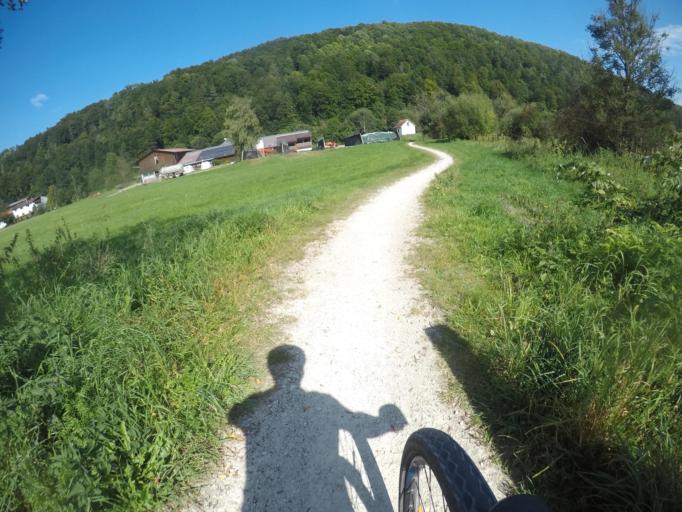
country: DE
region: Baden-Wuerttemberg
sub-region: Tuebingen Region
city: Mehrstetten
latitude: 48.3693
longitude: 9.6434
